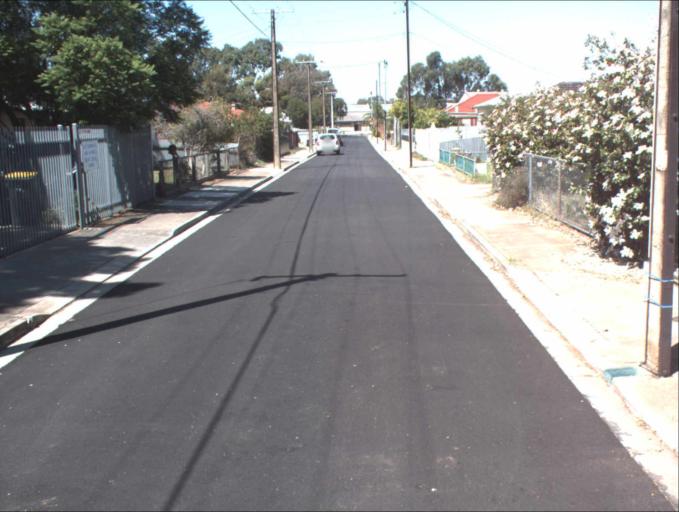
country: AU
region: South Australia
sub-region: Charles Sturt
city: Woodville North
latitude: -34.8491
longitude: 138.5492
